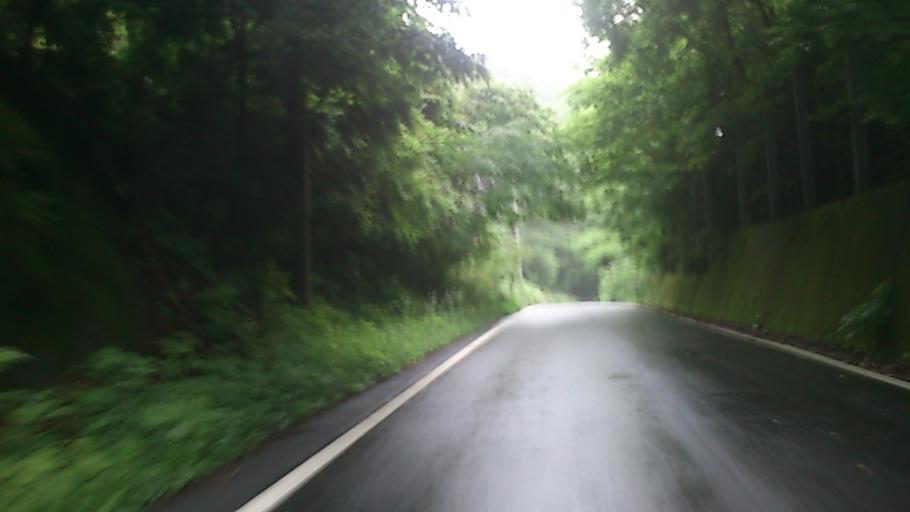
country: JP
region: Ibaraki
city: Omiya
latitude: 36.6275
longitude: 140.3672
